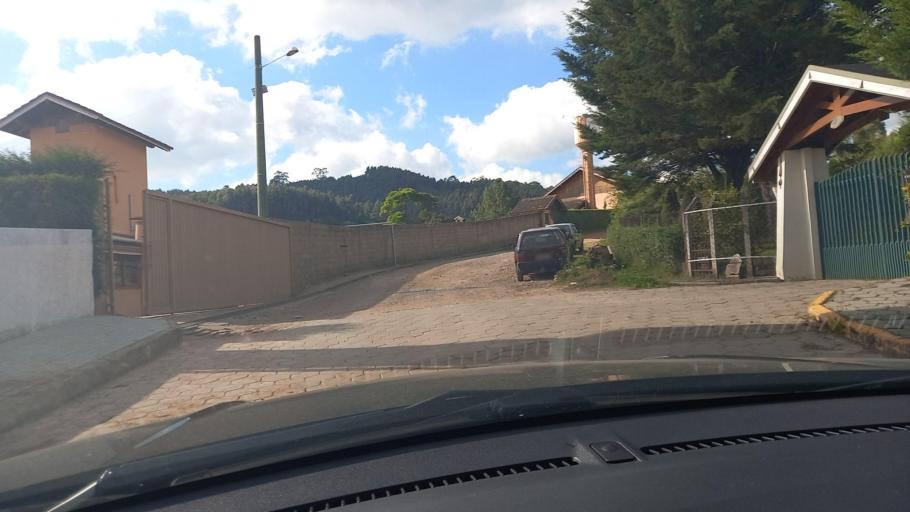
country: BR
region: Minas Gerais
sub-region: Camanducaia
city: Camanducaia
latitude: -22.8620
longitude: -46.0438
